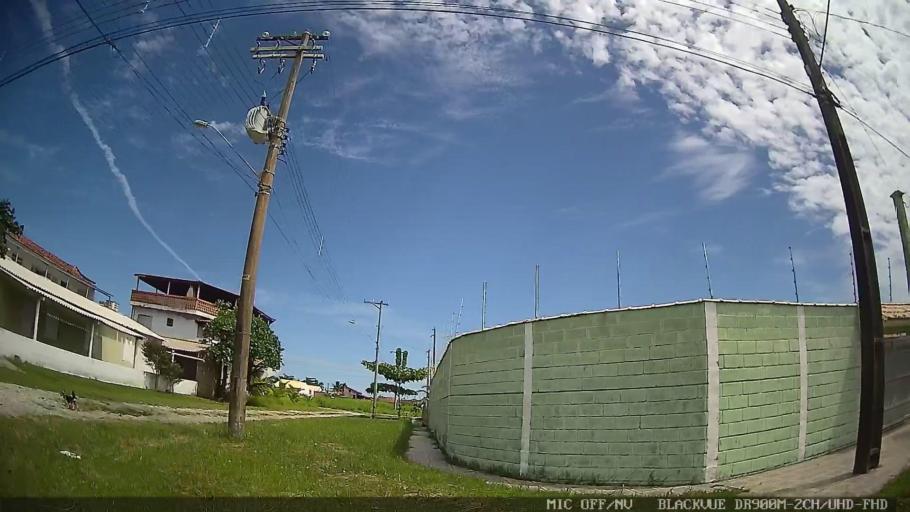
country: BR
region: Sao Paulo
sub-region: Iguape
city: Iguape
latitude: -24.7269
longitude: -47.5179
